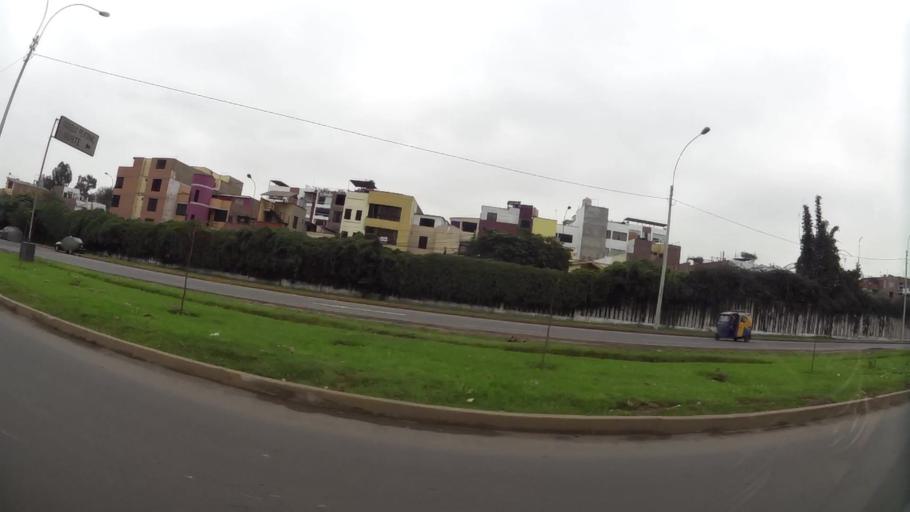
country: PE
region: Lima
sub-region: Lima
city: Vitarte
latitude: -12.0533
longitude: -76.9378
